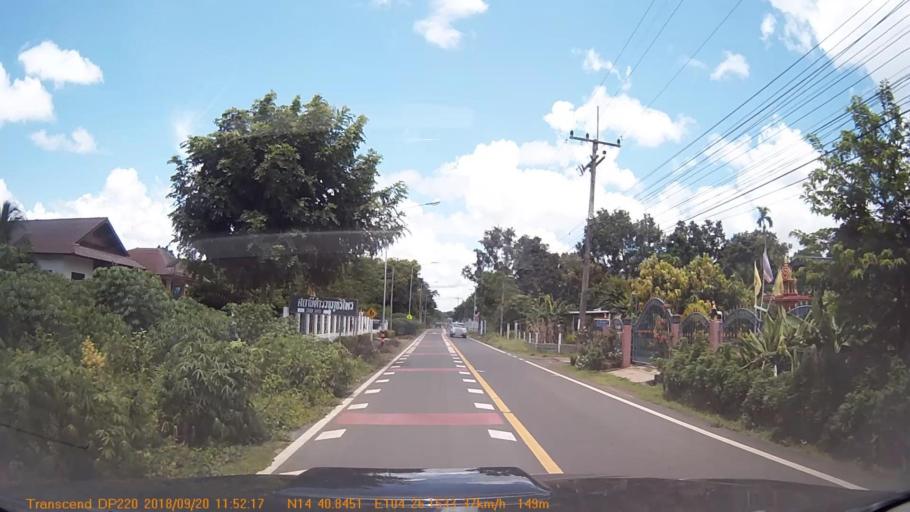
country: TH
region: Sisaket
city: Khun Han
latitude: 14.6812
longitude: 104.4358
